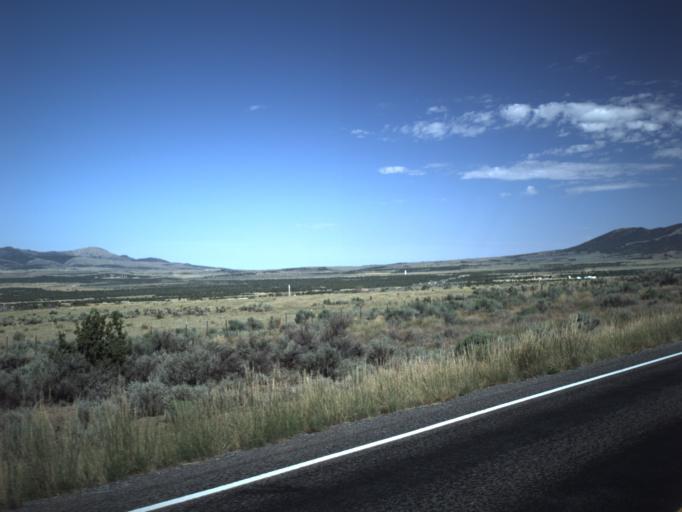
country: US
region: Utah
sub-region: Juab County
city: Mona
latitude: 39.9053
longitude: -112.1391
